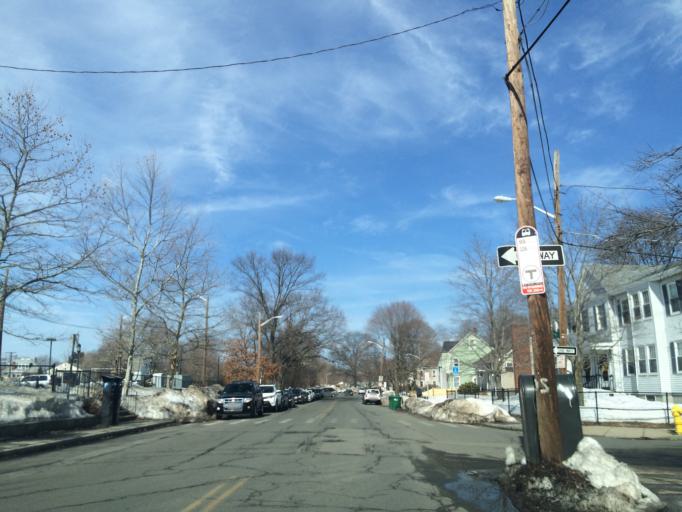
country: US
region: Massachusetts
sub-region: Middlesex County
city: Arlington
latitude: 42.4216
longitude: -71.1329
